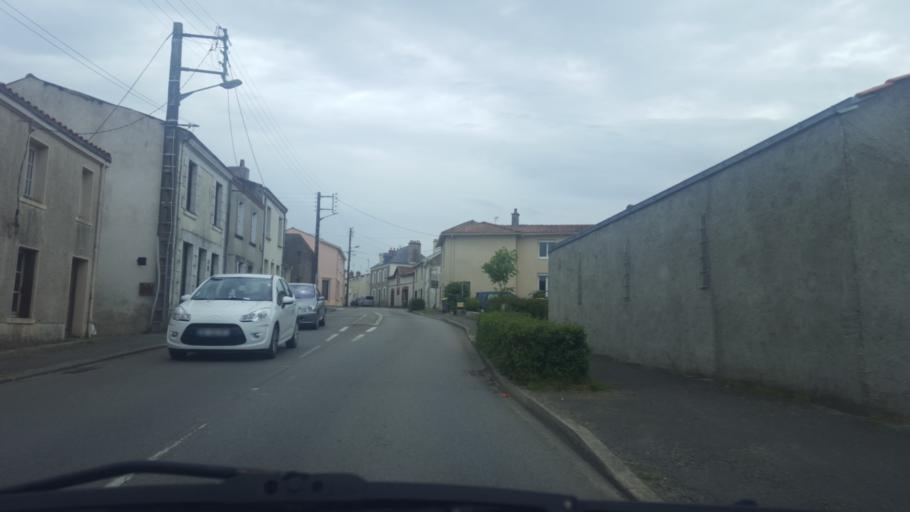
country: FR
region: Pays de la Loire
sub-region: Departement de la Loire-Atlantique
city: La Limouziniere
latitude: 47.0157
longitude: -1.5691
